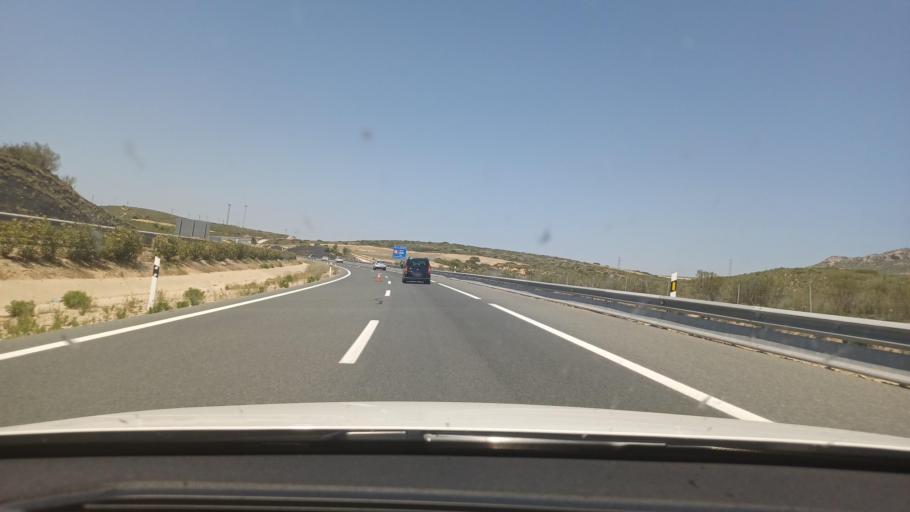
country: ES
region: Castille-La Mancha
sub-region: Provincia de Albacete
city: Almansa
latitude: 38.8776
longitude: -1.1868
